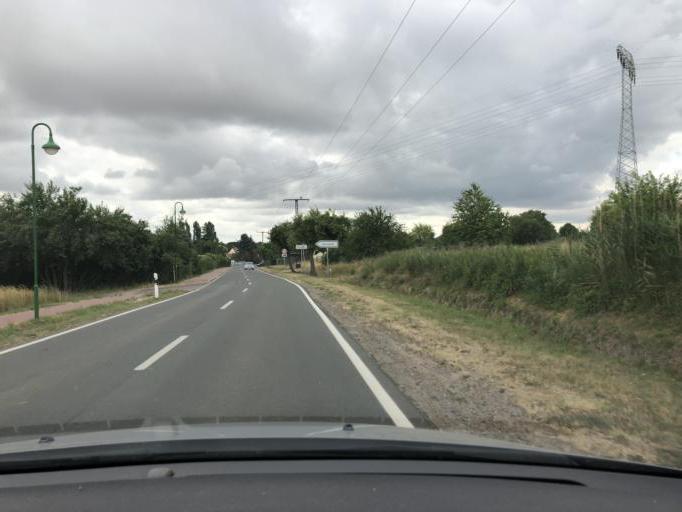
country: DE
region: Saxony-Anhalt
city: Ermlitz
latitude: 51.3898
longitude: 12.1522
